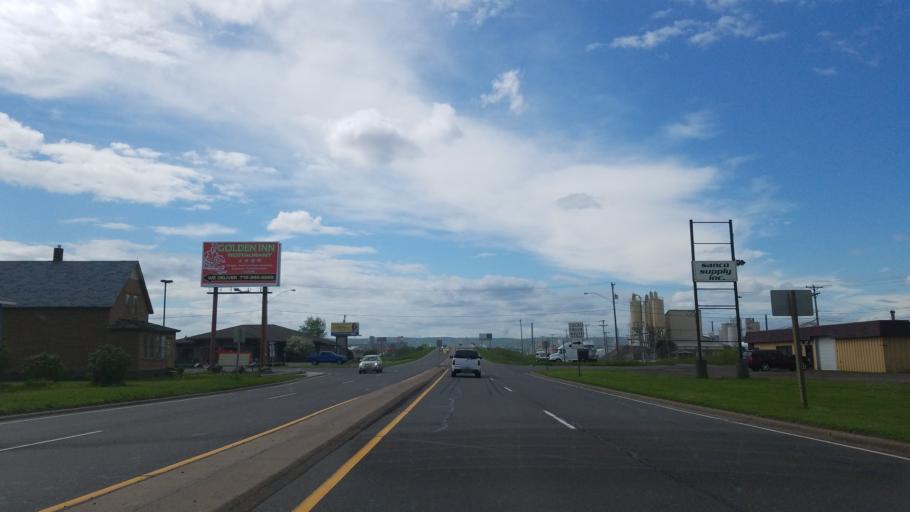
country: US
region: Wisconsin
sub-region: Douglas County
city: Superior
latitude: 46.7250
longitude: -92.0725
